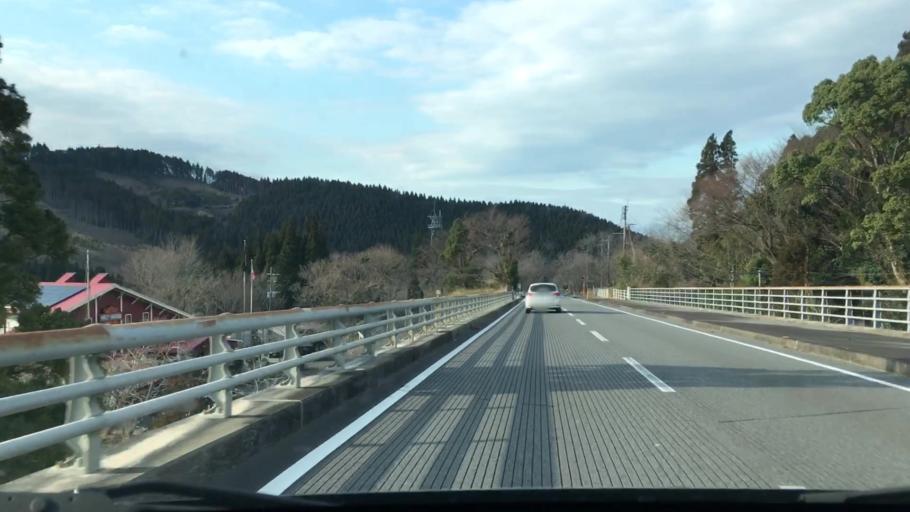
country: JP
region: Miyazaki
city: Miyazaki-shi
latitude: 31.8002
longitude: 131.3031
